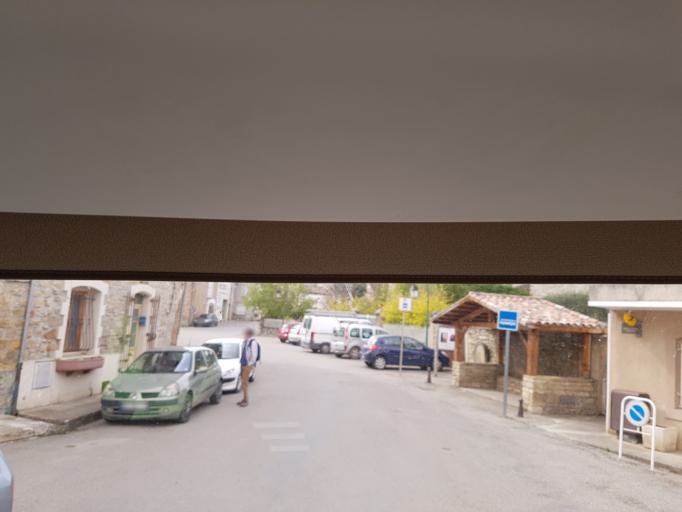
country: FR
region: Languedoc-Roussillon
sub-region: Departement de l'Aude
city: Esperaza
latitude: 42.9160
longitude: 2.2073
